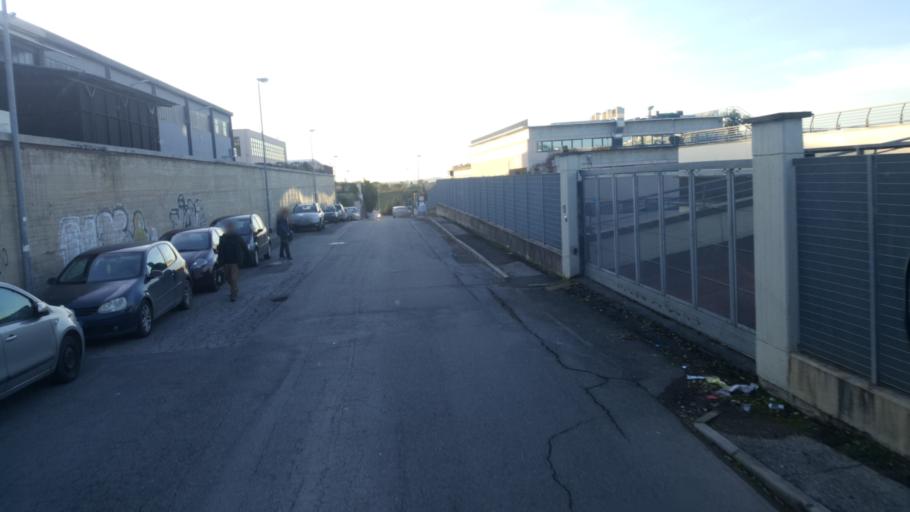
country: IT
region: Latium
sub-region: Citta metropolitana di Roma Capitale
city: Formello
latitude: 42.0514
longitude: 12.4028
